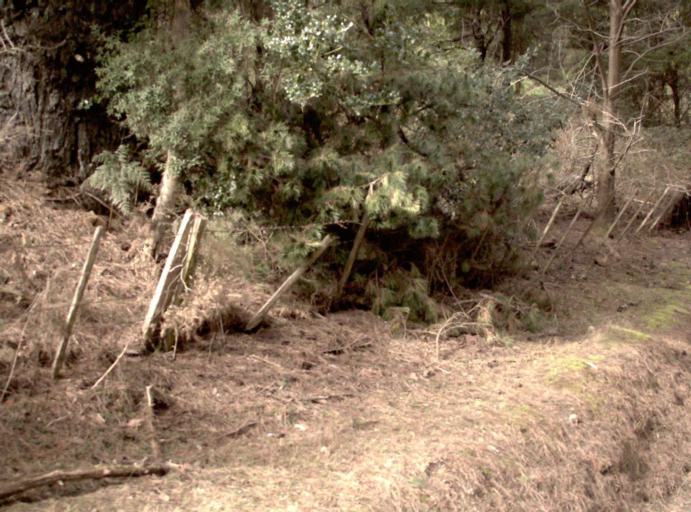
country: AU
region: Tasmania
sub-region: Launceston
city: Mayfield
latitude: -41.2761
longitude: 147.1876
